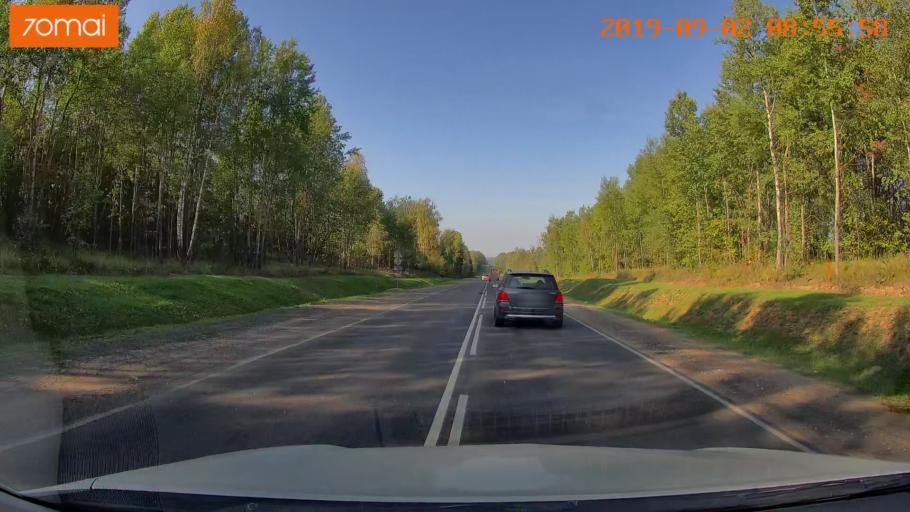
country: RU
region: Kaluga
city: Medyn'
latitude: 54.9492
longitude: 35.8037
